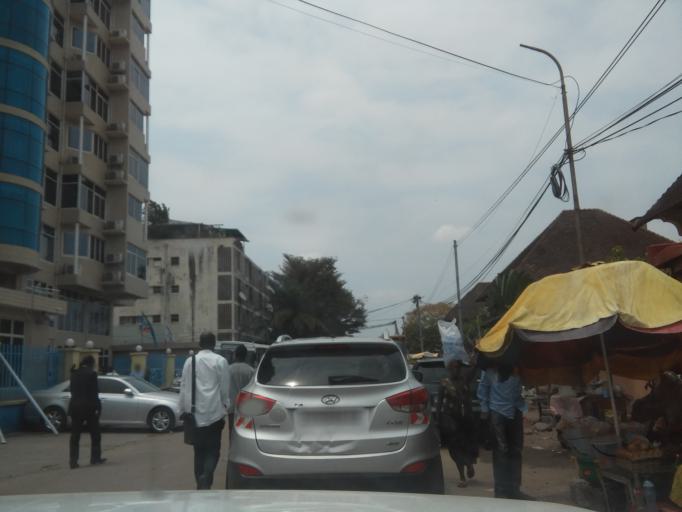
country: CD
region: Kinshasa
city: Kinshasa
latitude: -4.3069
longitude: 15.2995
